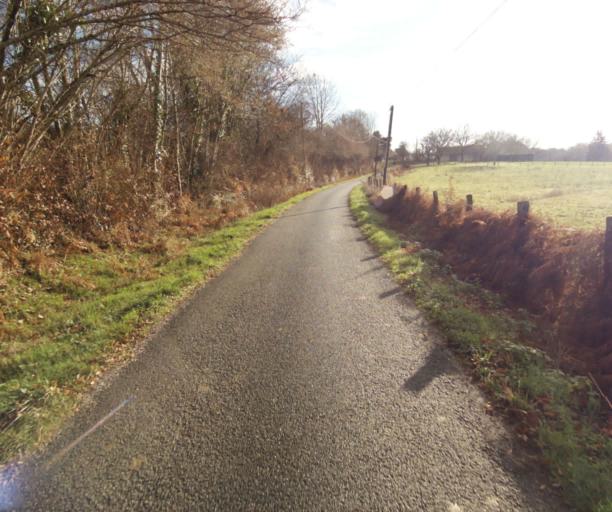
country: FR
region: Limousin
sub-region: Departement de la Correze
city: Sainte-Fereole
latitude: 45.2613
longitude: 1.6014
